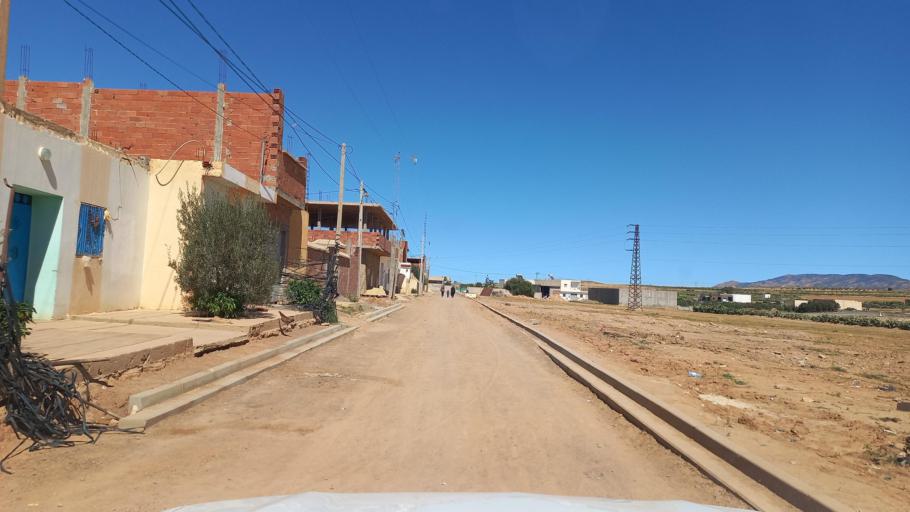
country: TN
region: Al Qasrayn
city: Sbiba
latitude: 35.3602
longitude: 9.0914
